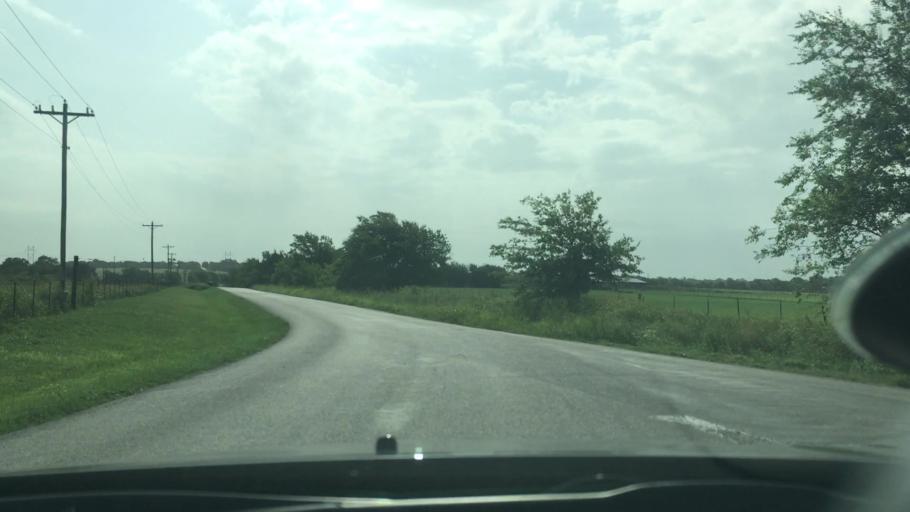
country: US
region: Oklahoma
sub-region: Carter County
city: Lone Grove
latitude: 34.2166
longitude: -97.2728
